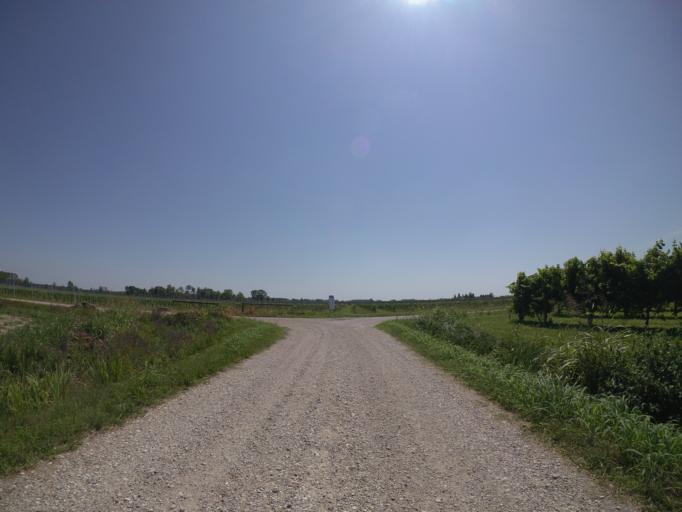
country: IT
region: Friuli Venezia Giulia
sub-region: Provincia di Udine
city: Varmo
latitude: 45.9206
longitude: 13.0037
